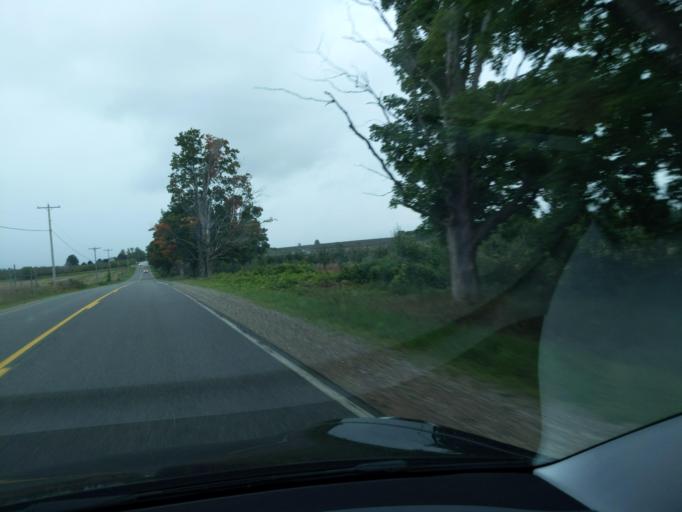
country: US
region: Michigan
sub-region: Antrim County
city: Elk Rapids
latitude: 44.8267
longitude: -85.4050
